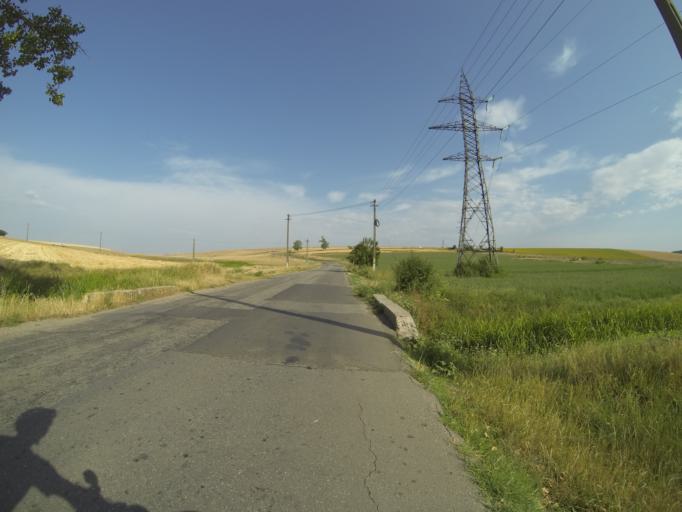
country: RO
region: Dolj
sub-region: Comuna Dranicu
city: Padea
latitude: 44.0336
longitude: 23.8562
